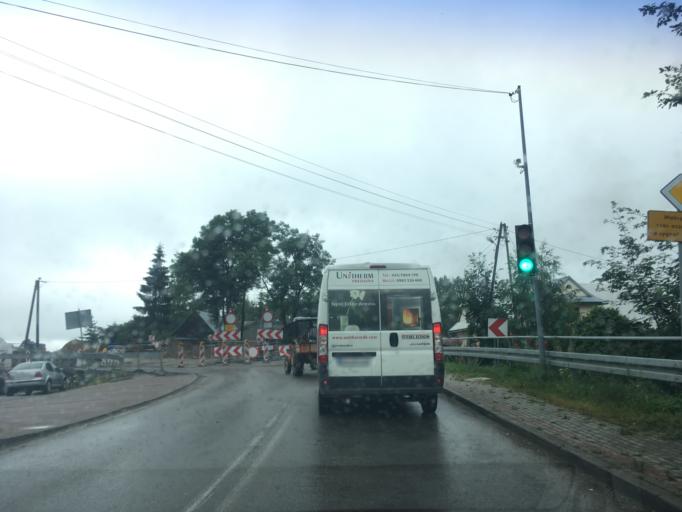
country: PL
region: Lesser Poland Voivodeship
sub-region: Powiat nowotarski
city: Czarny Dunajec
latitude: 49.3950
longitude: 19.8194
